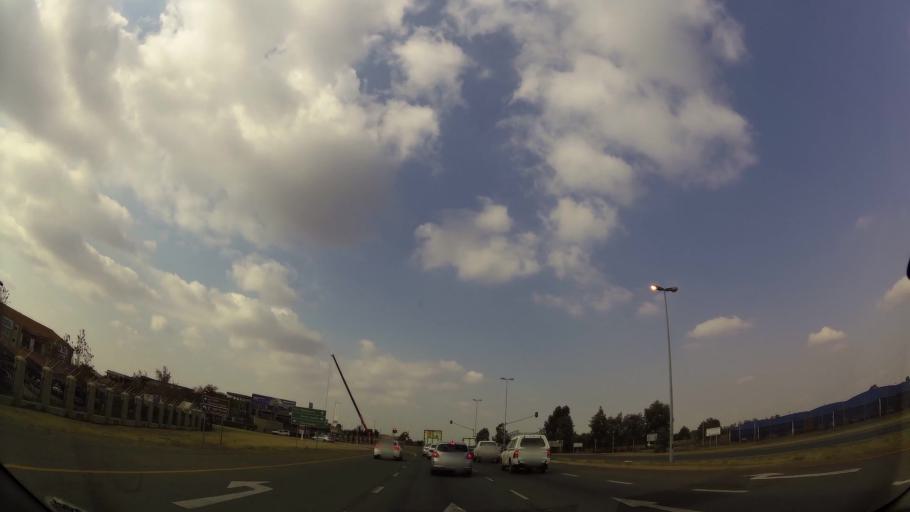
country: ZA
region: Gauteng
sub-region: Ekurhuleni Metropolitan Municipality
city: Benoni
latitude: -26.1486
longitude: 28.2714
